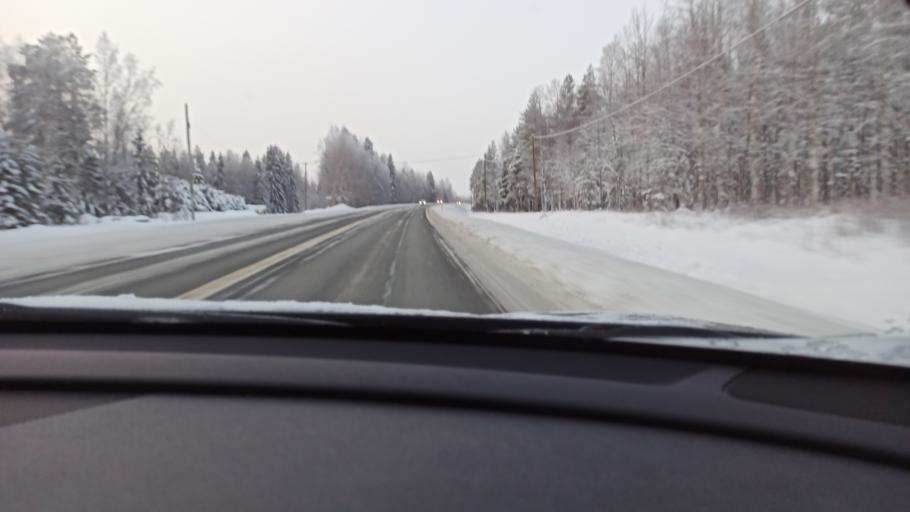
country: FI
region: Lapland
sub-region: Rovaniemi
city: Rovaniemi
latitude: 66.5515
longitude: 25.8925
